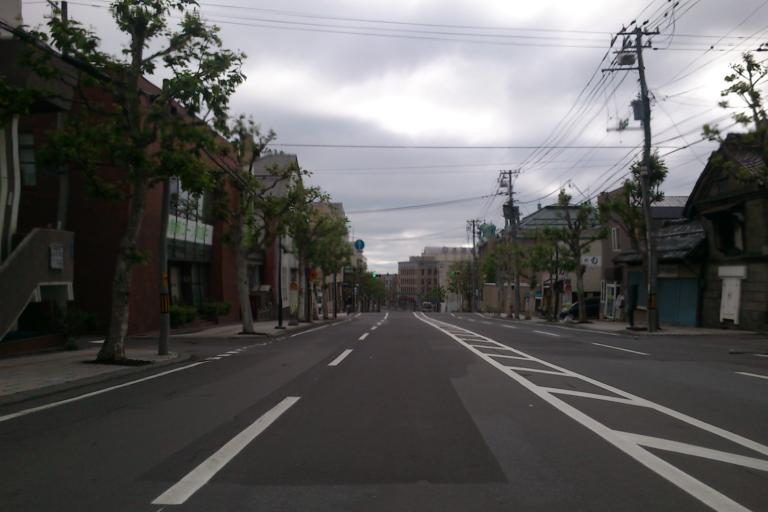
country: JP
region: Hokkaido
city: Otaru
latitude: 43.1958
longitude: 140.9978
